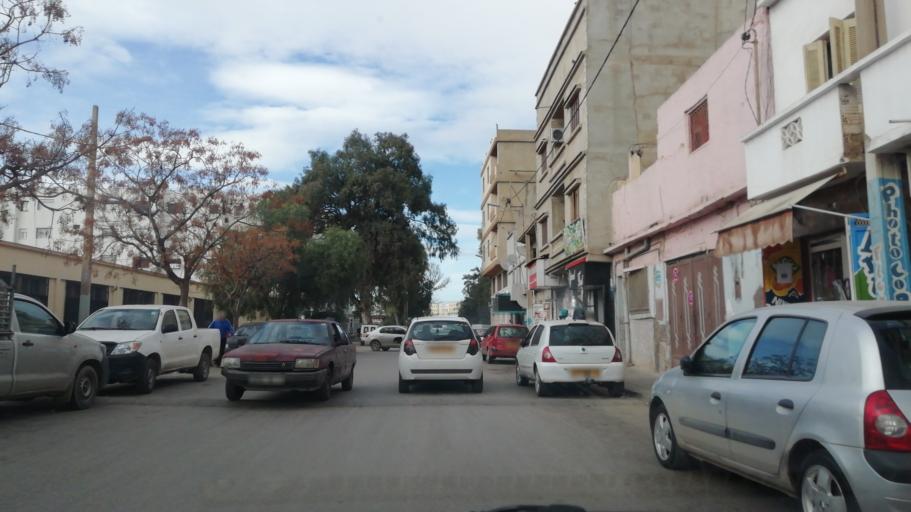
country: DZ
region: Oran
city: Oran
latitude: 35.6837
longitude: -0.6026
